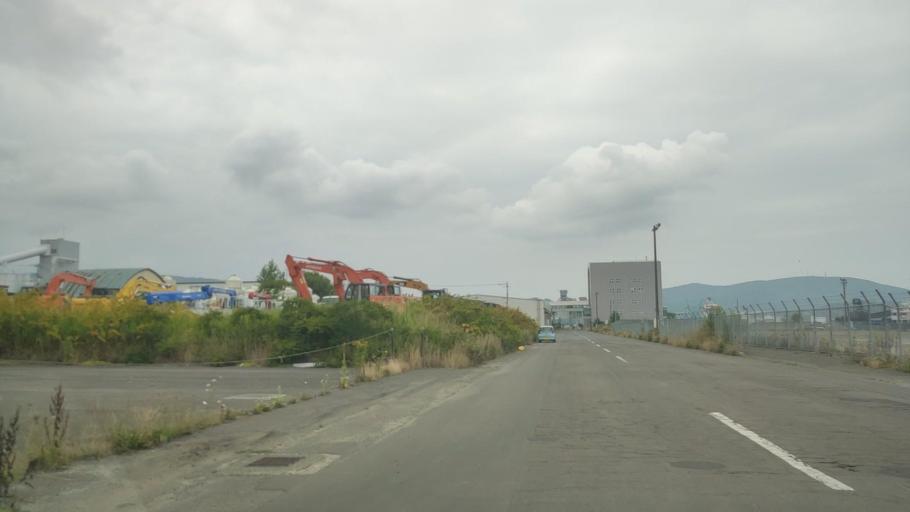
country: JP
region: Hokkaido
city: Otaru
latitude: 43.1888
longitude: 141.0215
